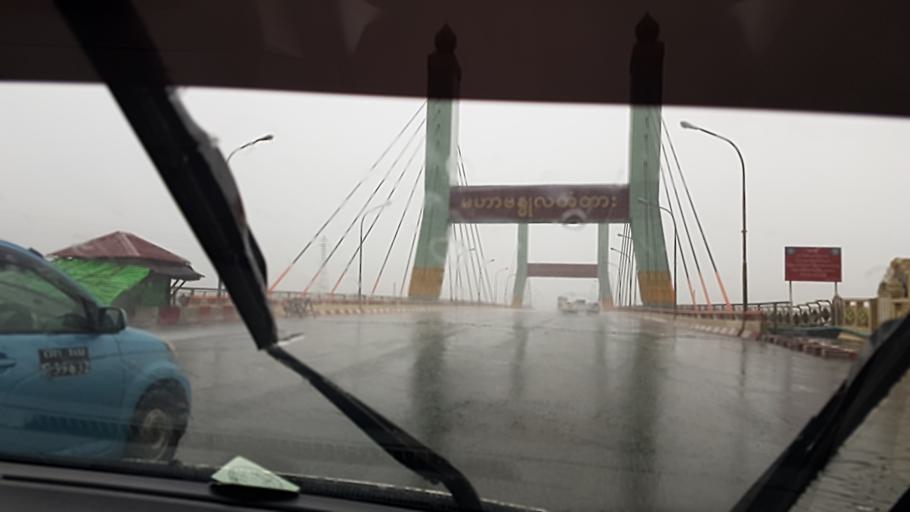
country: MM
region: Yangon
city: Yangon
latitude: 16.7757
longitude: 96.1827
